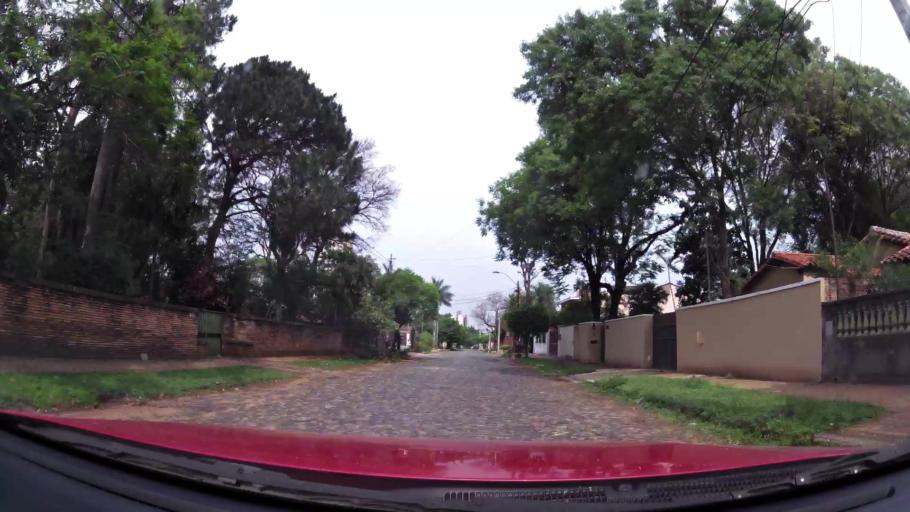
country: PY
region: Central
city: Fernando de la Mora
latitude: -25.2892
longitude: -57.5587
